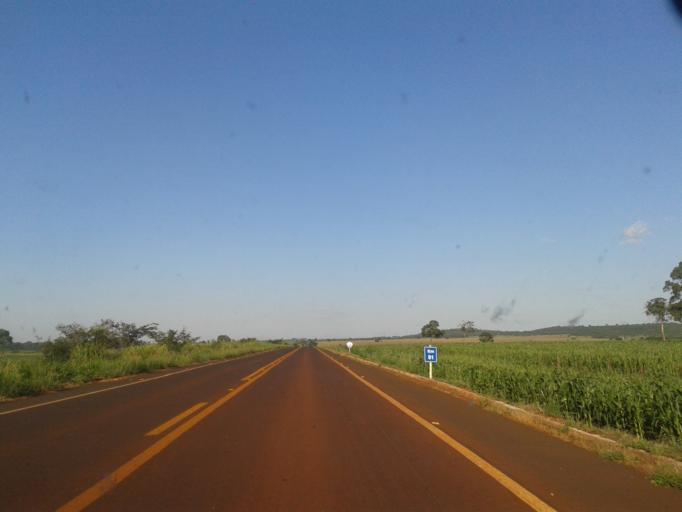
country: BR
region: Minas Gerais
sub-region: Capinopolis
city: Capinopolis
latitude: -18.7121
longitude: -49.8330
